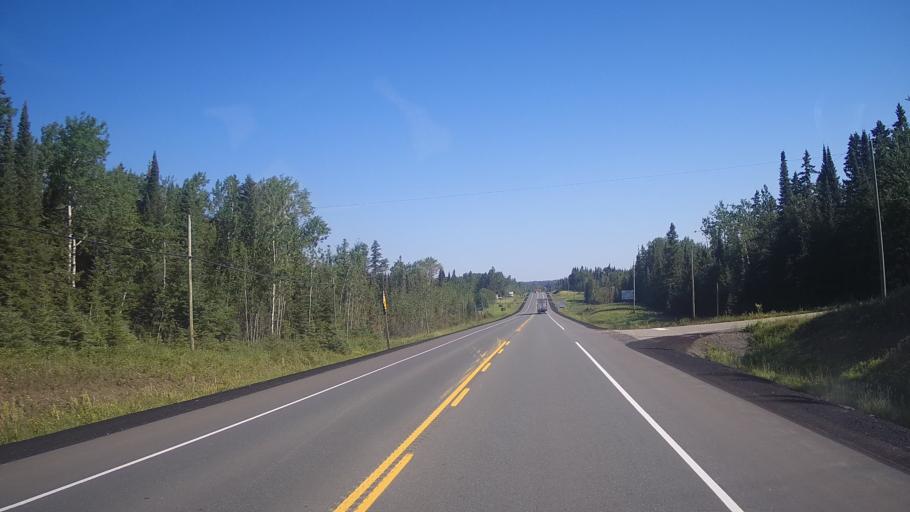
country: CA
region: Ontario
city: Dryden
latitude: 49.6728
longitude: -92.4926
